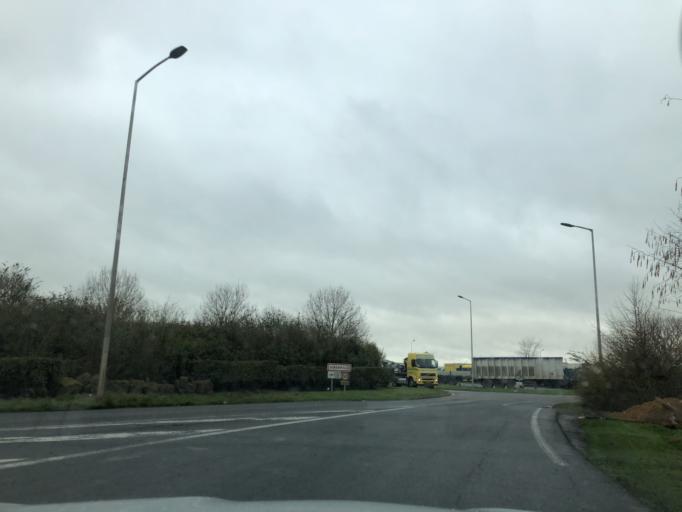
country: FR
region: Lower Normandy
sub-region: Departement du Calvados
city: Giberville
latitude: 49.1724
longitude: -0.2947
